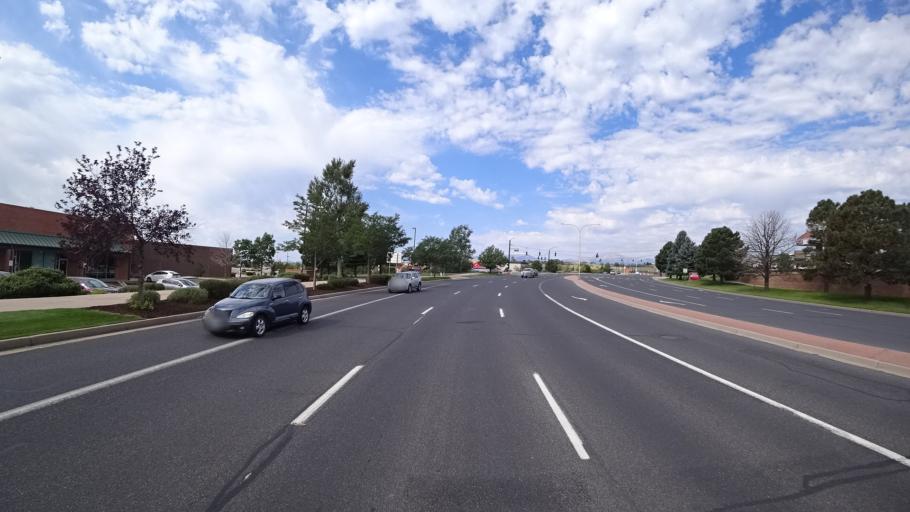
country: US
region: Colorado
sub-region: El Paso County
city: Cimarron Hills
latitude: 38.8939
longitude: -104.7157
